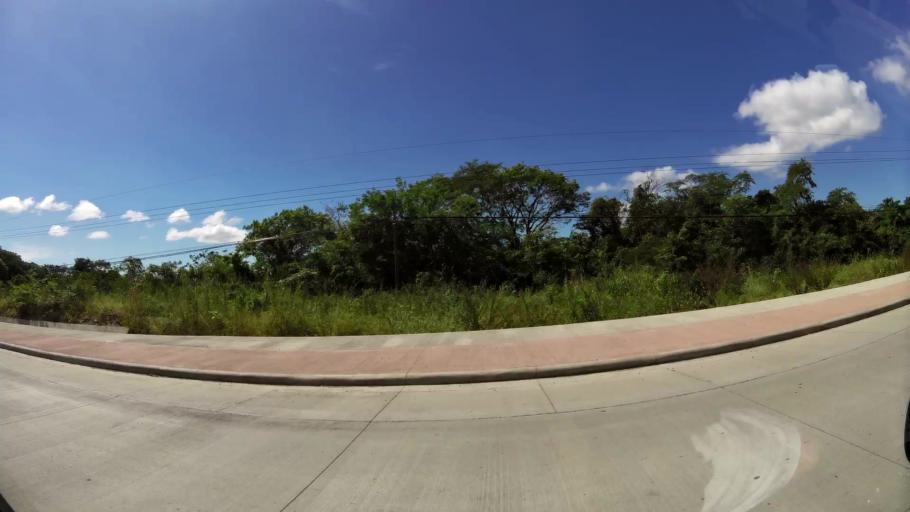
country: CR
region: Guanacaste
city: Bagaces
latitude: 10.5140
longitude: -85.2382
